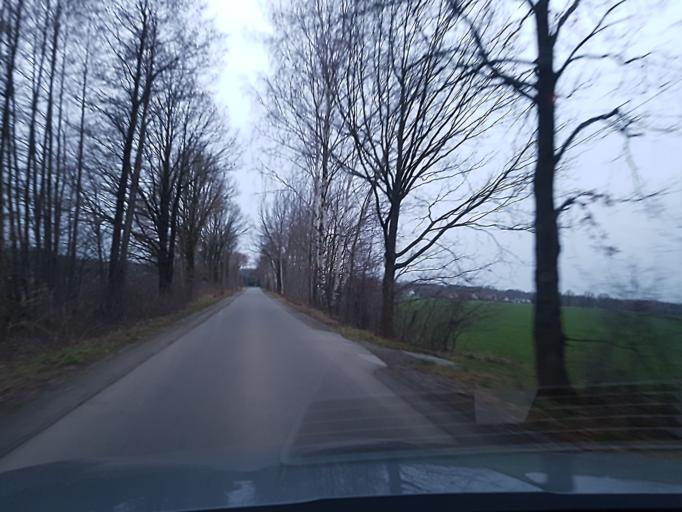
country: DE
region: Brandenburg
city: Schonewalde
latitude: 51.6431
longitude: 13.6119
